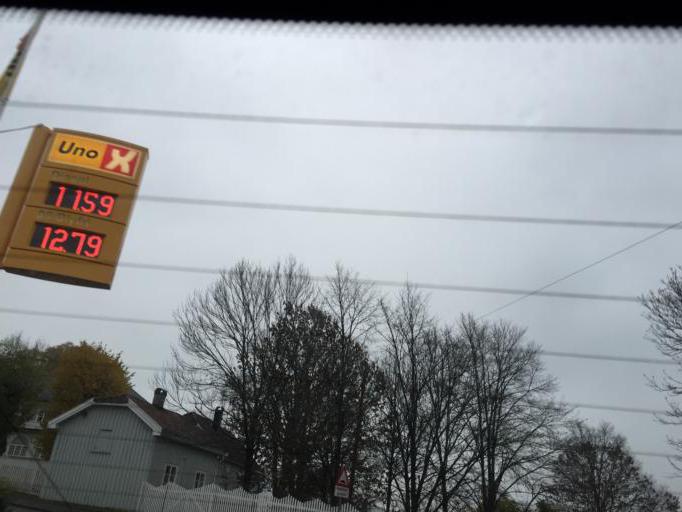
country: NO
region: Buskerud
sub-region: Drammen
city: Drammen
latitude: 59.7293
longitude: 10.2061
